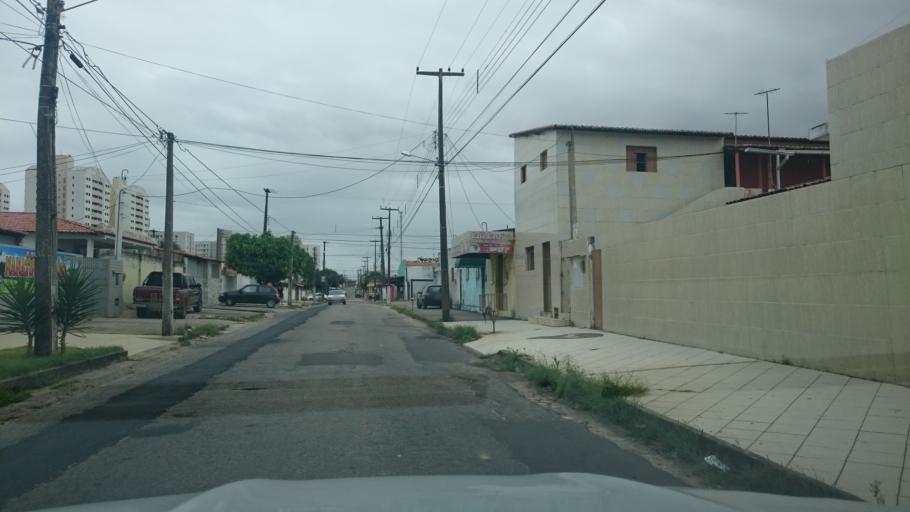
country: BR
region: Rio Grande do Norte
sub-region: Parnamirim
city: Parnamirim
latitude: -5.8746
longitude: -35.2119
